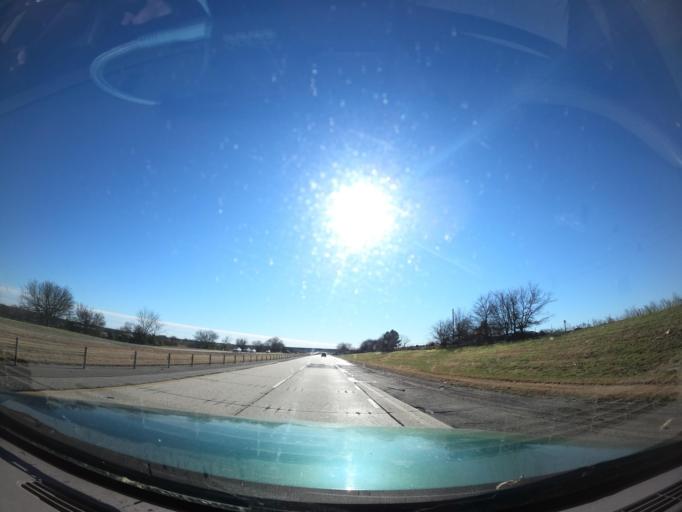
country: US
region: Oklahoma
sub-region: McIntosh County
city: Checotah
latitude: 35.4526
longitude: -95.5470
